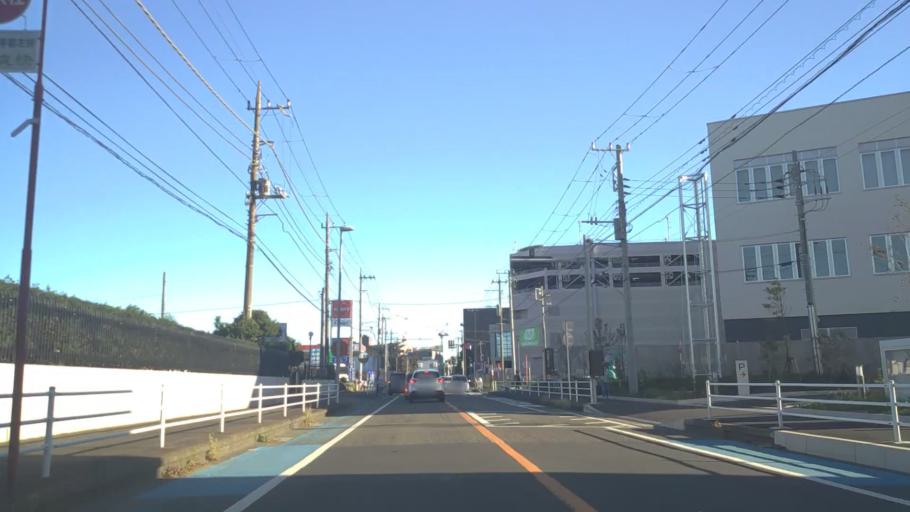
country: JP
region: Kanagawa
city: Chigasaki
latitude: 35.3376
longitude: 139.4029
